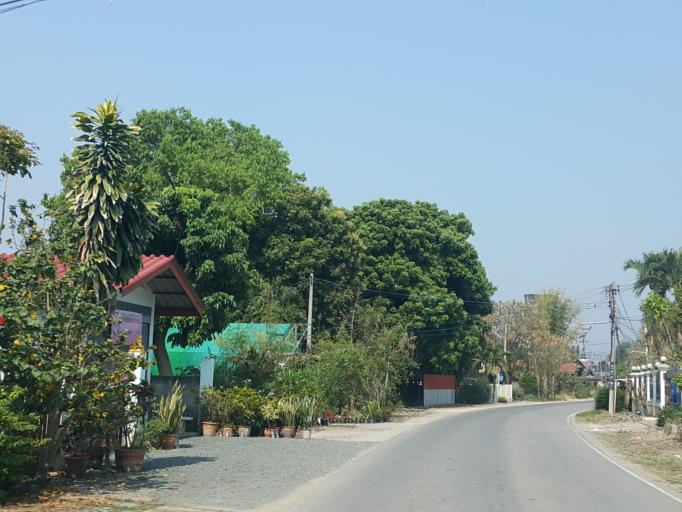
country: TH
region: Chiang Mai
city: San Kamphaeng
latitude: 18.7366
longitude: 99.1103
